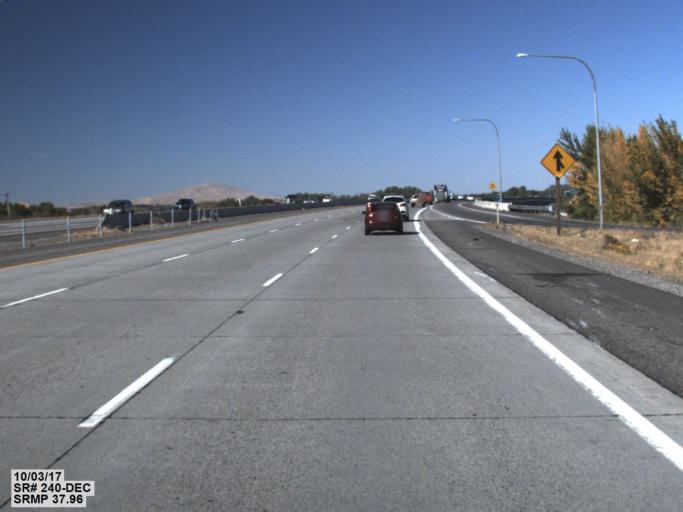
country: US
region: Washington
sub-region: Franklin County
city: West Pasco
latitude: 46.2366
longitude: -119.2407
